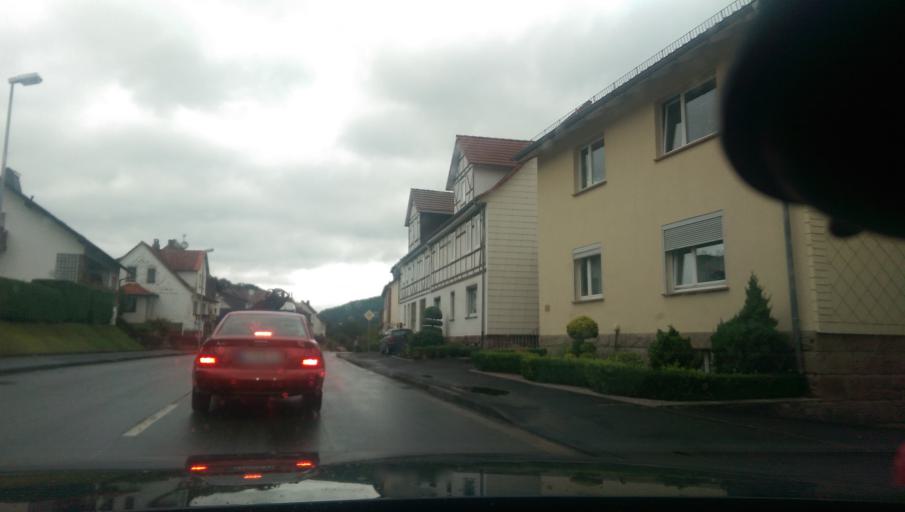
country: DE
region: Hesse
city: Witzenhausen
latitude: 51.2948
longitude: 9.8479
